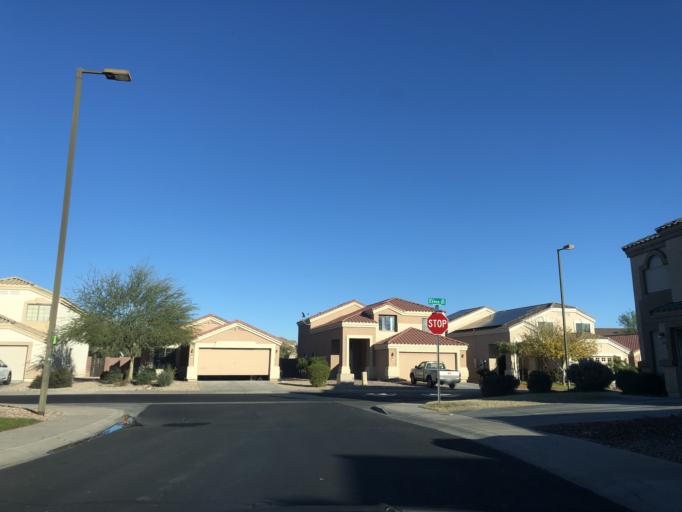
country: US
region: Arizona
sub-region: Maricopa County
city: Buckeye
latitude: 33.4370
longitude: -112.5657
